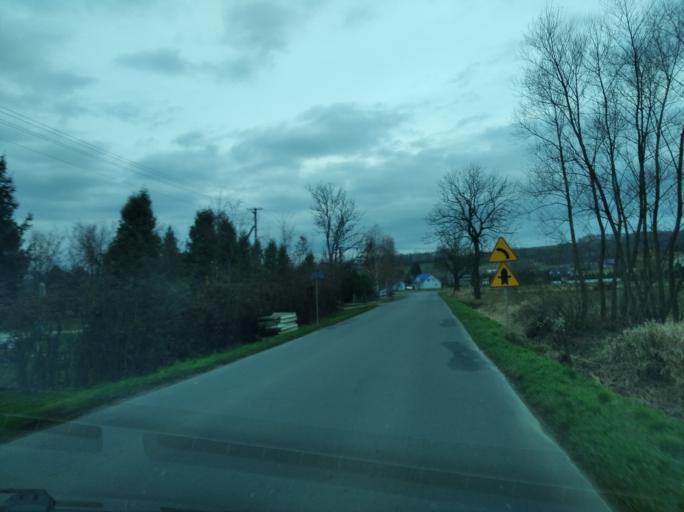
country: PL
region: Subcarpathian Voivodeship
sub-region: Powiat ropczycko-sedziszowski
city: Iwierzyce
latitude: 50.0369
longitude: 21.7462
